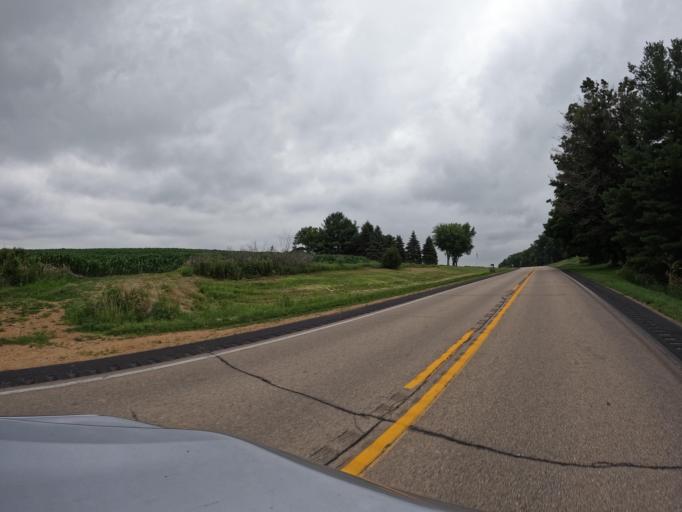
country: US
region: Illinois
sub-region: Carroll County
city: Savanna
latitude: 42.0082
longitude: -90.1841
